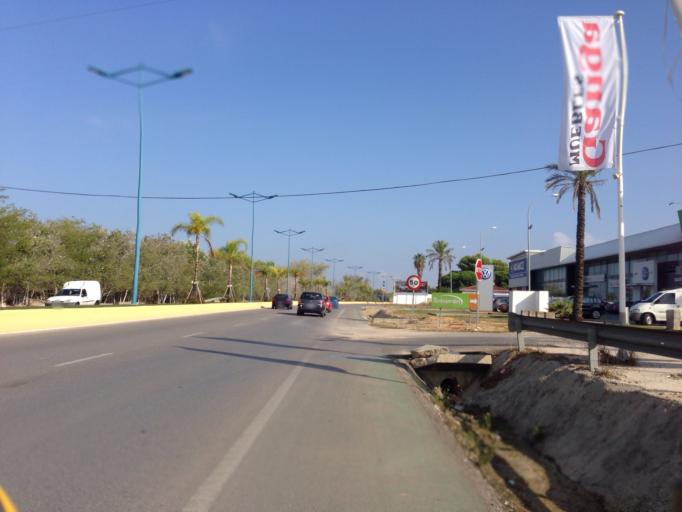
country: ES
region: Andalusia
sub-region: Provincia de Cadiz
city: Chiclana de la Frontera
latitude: 36.4370
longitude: -6.1439
